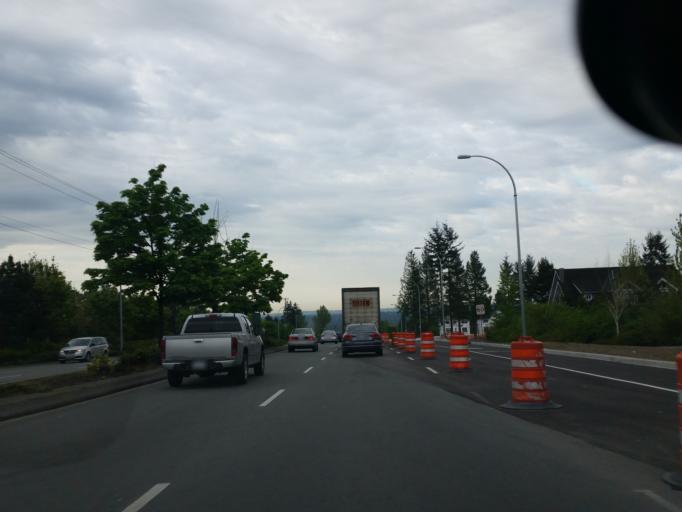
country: CA
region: British Columbia
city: Langley
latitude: 49.1327
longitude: -122.6685
